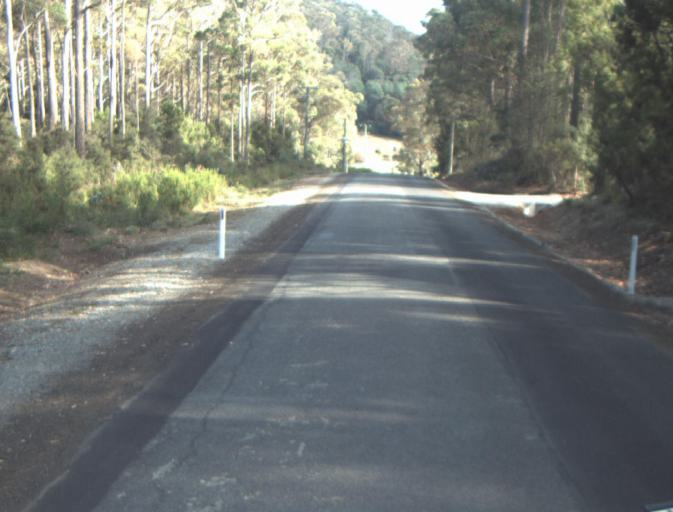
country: AU
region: Tasmania
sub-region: Launceston
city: Mayfield
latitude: -41.3065
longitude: 147.1988
